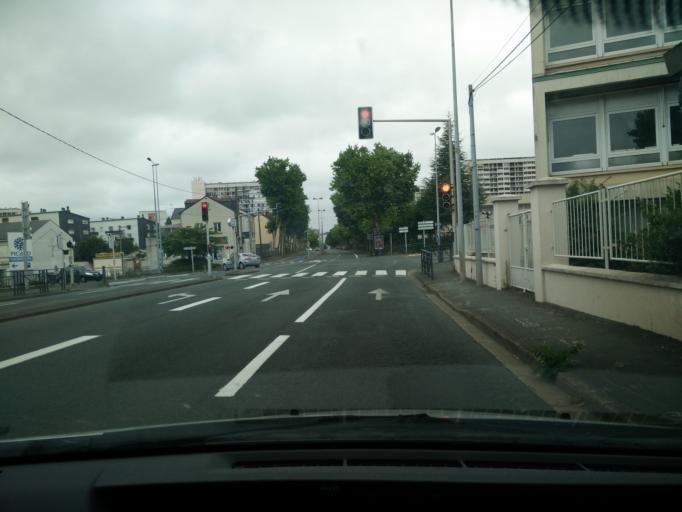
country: FR
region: Pays de la Loire
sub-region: Departement de Maine-et-Loire
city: Angers
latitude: 47.4687
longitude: -0.5314
